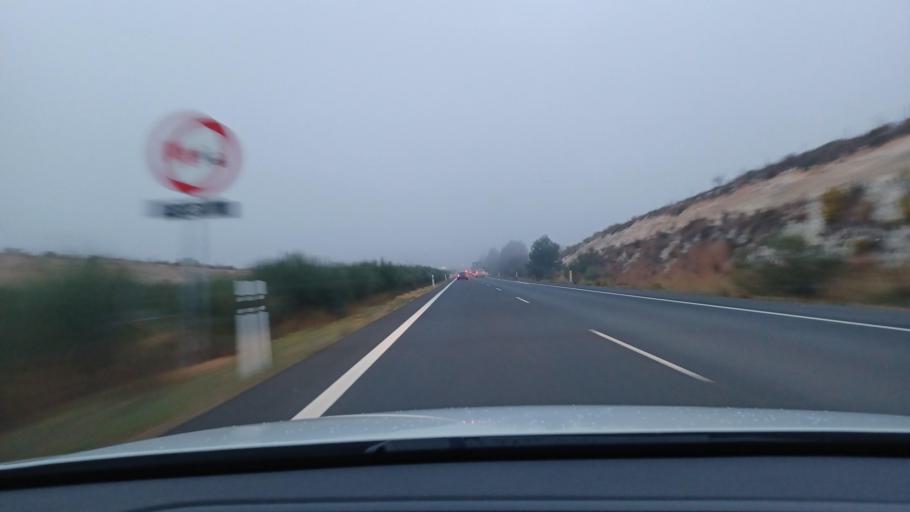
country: ES
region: Valencia
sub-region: Provincia de Valencia
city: Mogente
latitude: 38.8631
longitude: -0.7972
